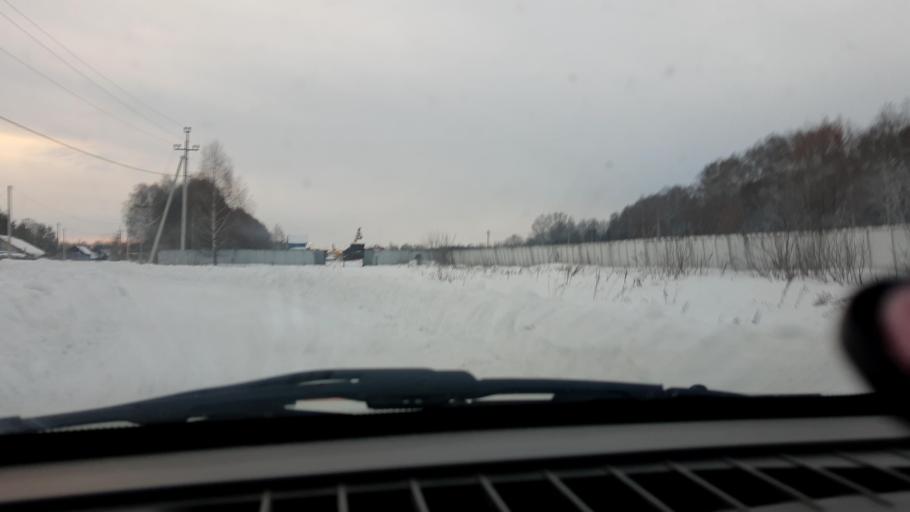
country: RU
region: Bashkortostan
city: Urman
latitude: 54.8744
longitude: 56.8670
